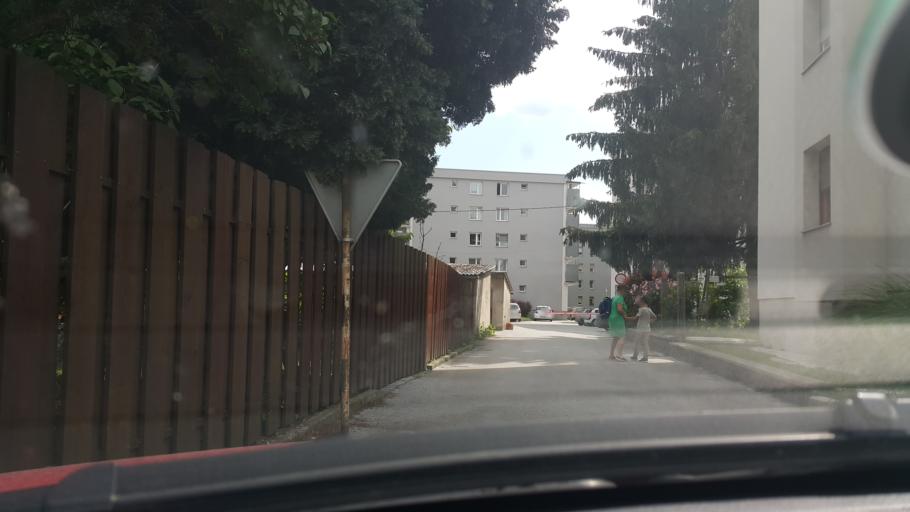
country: SI
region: Maribor
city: Maribor
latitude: 46.5644
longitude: 15.6371
